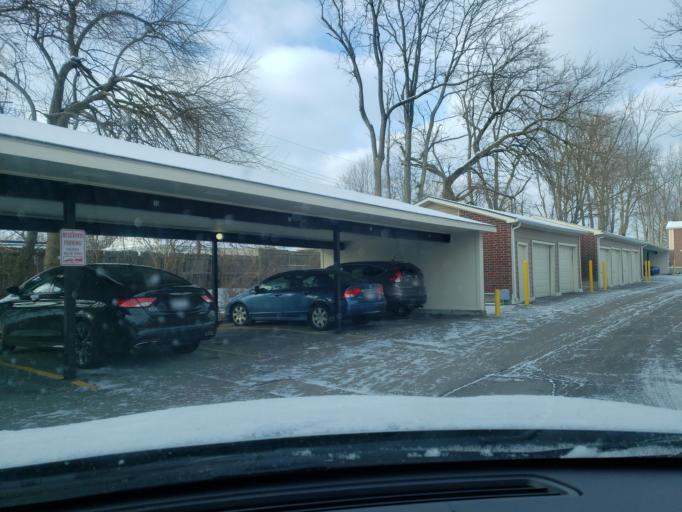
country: US
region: Ohio
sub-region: Montgomery County
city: Kettering
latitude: 39.6949
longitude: -84.1548
